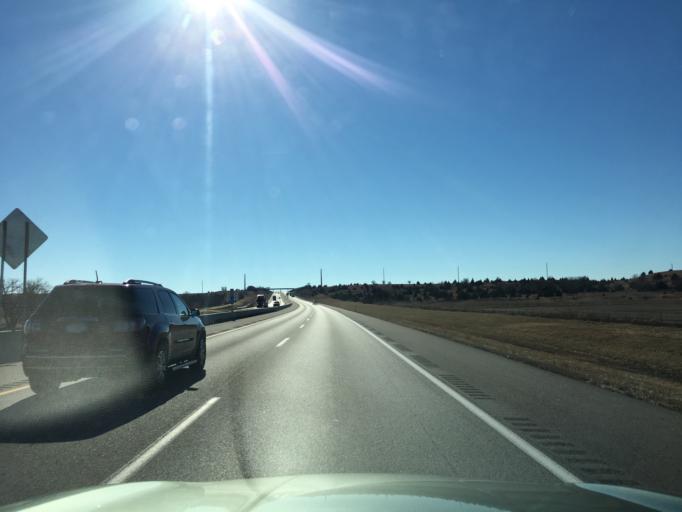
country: US
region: Kansas
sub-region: Sumner County
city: Wellington
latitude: 37.2134
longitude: -97.3398
